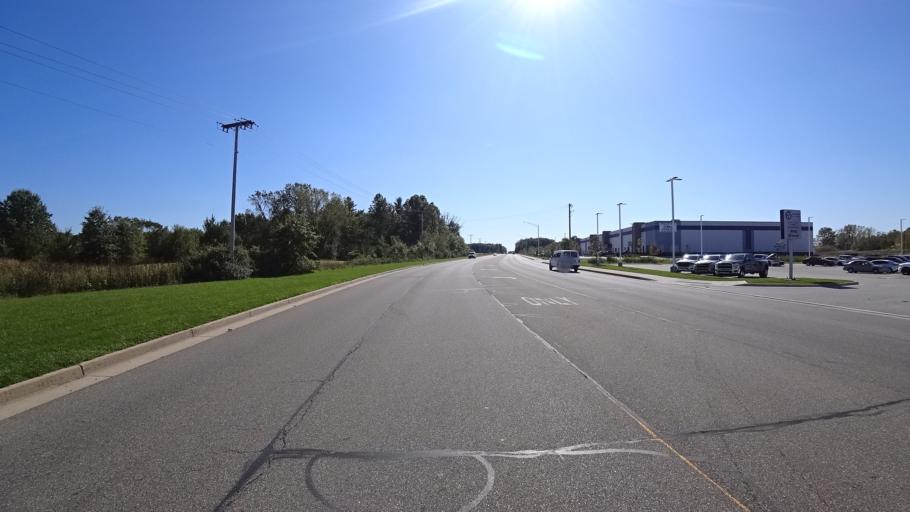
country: US
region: Indiana
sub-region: LaPorte County
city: Michigan City
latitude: 41.6797
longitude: -86.8845
